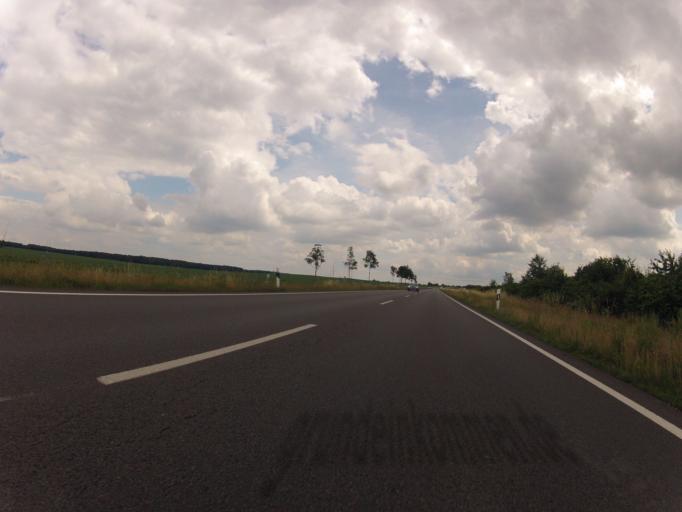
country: DE
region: Saxony
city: Brandis
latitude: 51.3618
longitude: 12.5852
